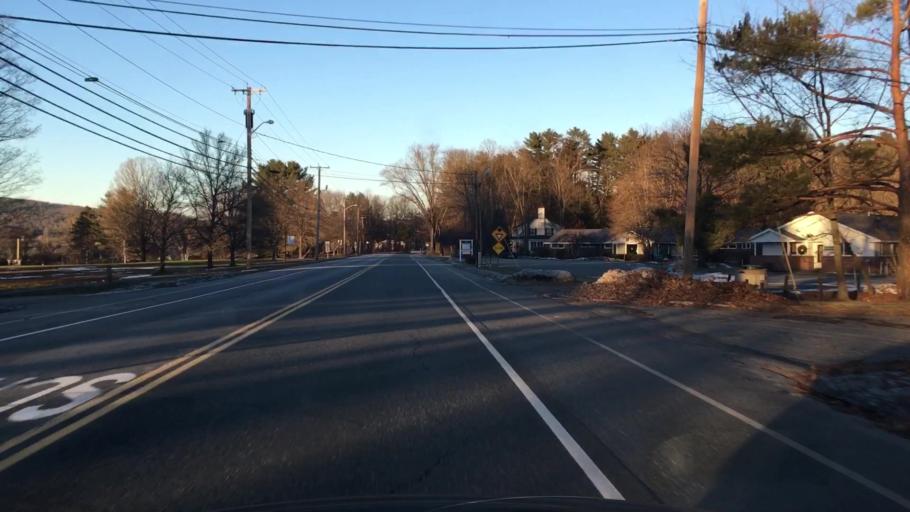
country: US
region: New Hampshire
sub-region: Grafton County
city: Hanover
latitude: 43.7257
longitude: -72.2696
